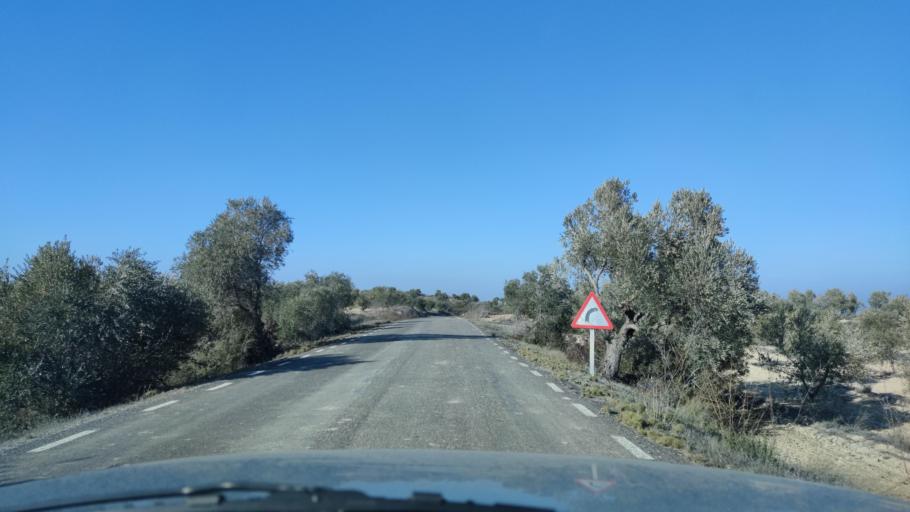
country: ES
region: Catalonia
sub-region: Provincia de Lleida
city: Torrebesses
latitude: 41.4309
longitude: 0.5678
